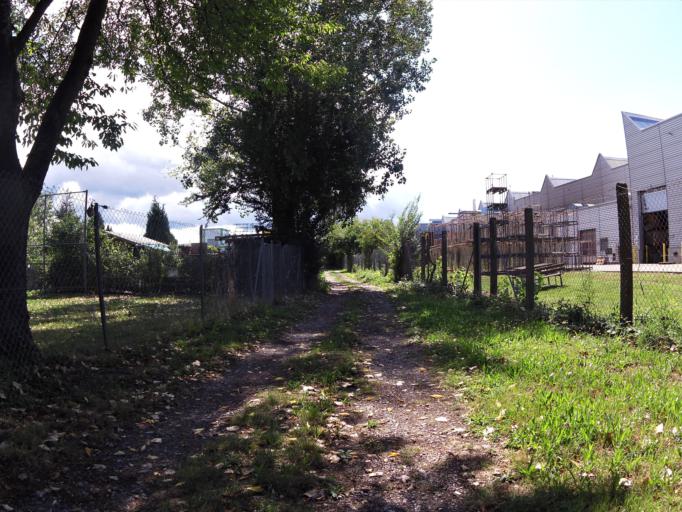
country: DE
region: Baden-Wuerttemberg
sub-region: Freiburg Region
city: Lahr
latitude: 48.3534
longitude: 7.8307
